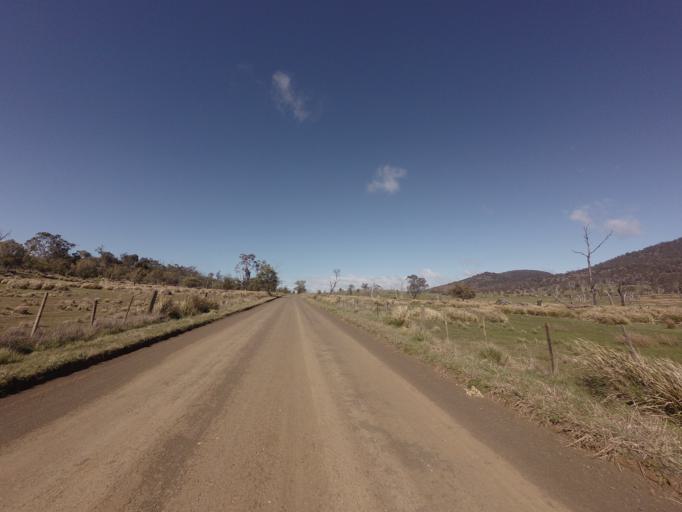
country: AU
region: Tasmania
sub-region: Northern Midlands
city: Evandale
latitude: -41.9357
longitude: 147.4195
